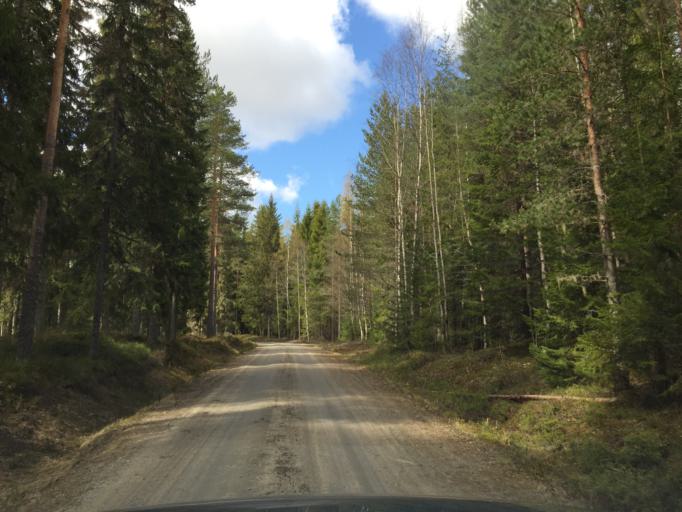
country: SE
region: Gaevleborg
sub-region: Bollnas Kommun
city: Arbra
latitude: 61.5239
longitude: 16.3129
